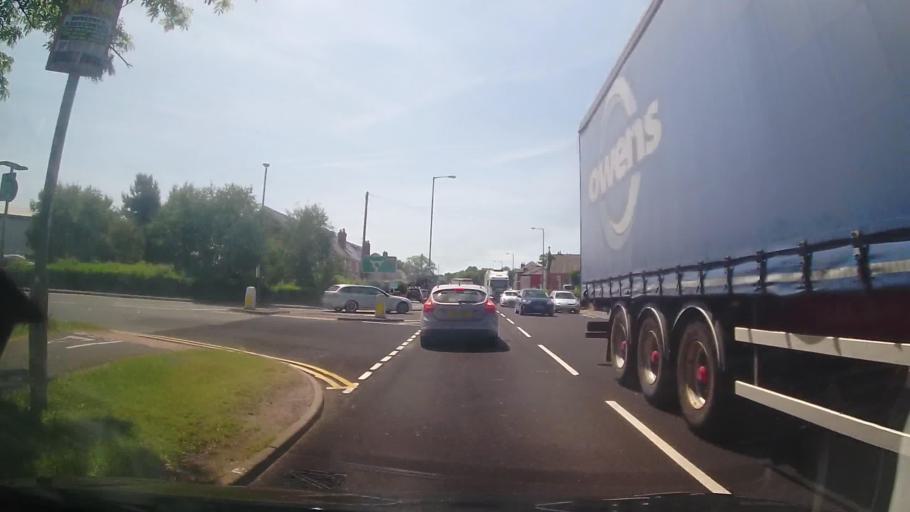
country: GB
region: England
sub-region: Herefordshire
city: Hereford
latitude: 52.0676
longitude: -2.7220
